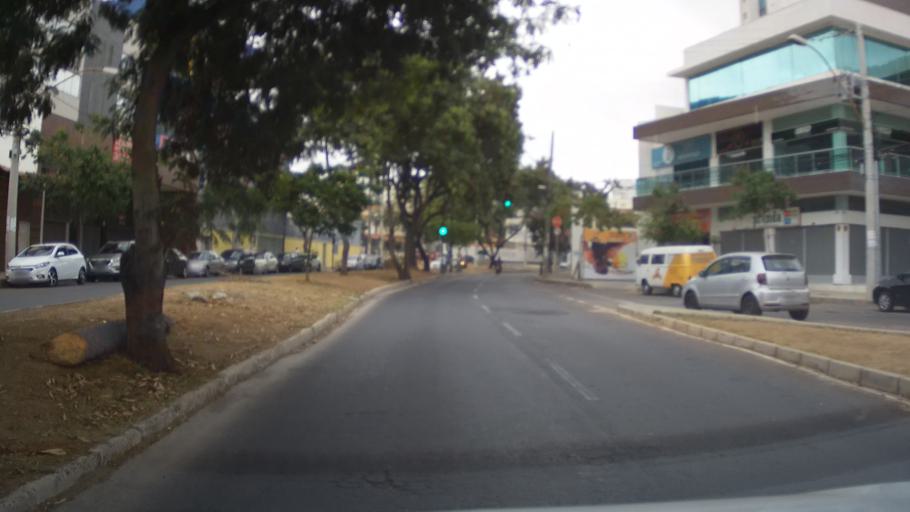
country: BR
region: Minas Gerais
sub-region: Belo Horizonte
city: Belo Horizonte
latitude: -19.8617
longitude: -43.9392
